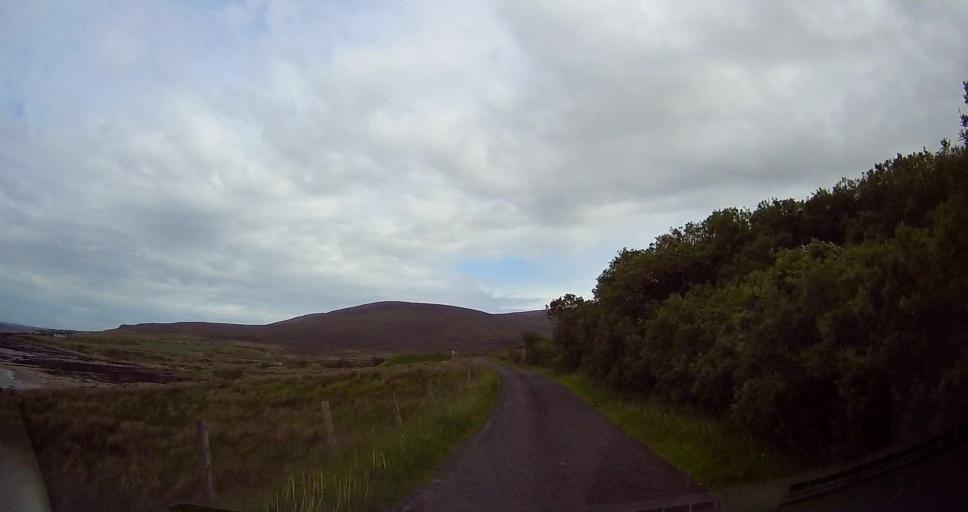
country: GB
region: Scotland
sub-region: Orkney Islands
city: Stromness
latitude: 58.9078
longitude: -3.3188
